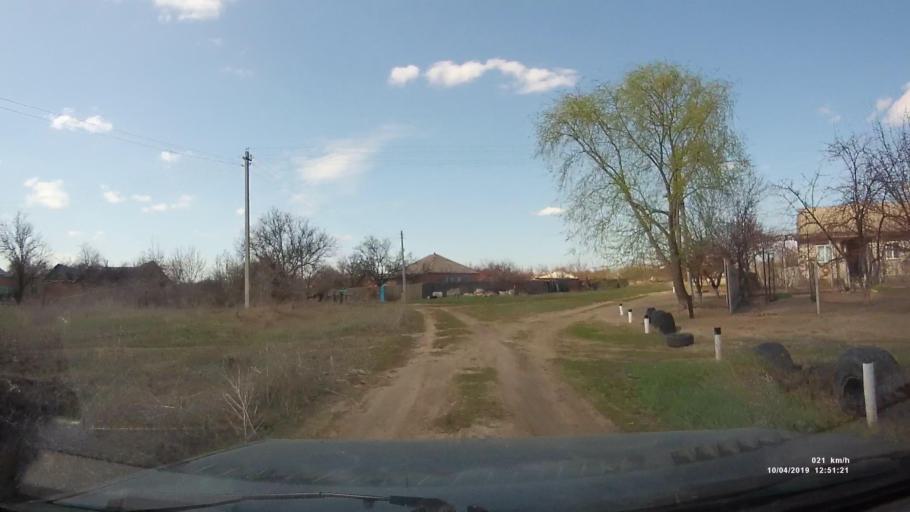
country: RU
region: Rostov
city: Kamensk-Shakhtinskiy
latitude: 48.3592
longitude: 40.2175
